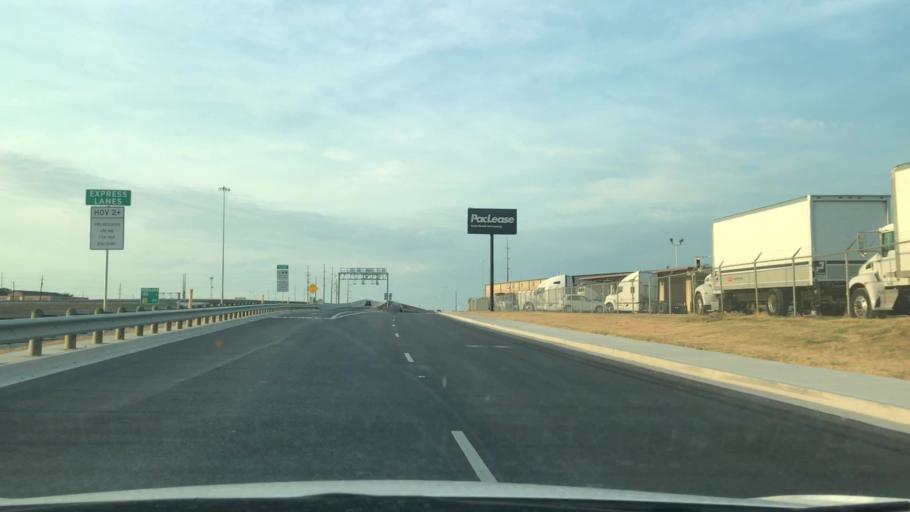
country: US
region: Texas
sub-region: Tarrant County
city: Haltom City
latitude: 32.7979
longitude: -97.3209
